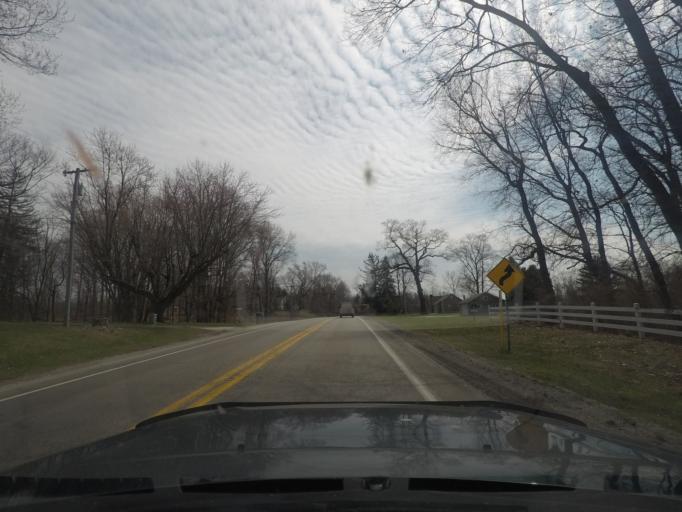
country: US
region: Indiana
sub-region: LaPorte County
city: LaPorte
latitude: 41.6429
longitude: -86.7476
